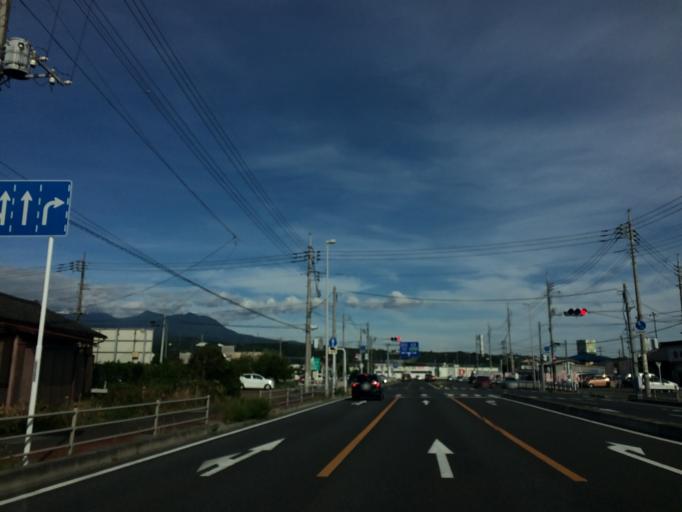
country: JP
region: Gunma
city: Shibukawa
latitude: 36.4825
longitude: 139.0109
